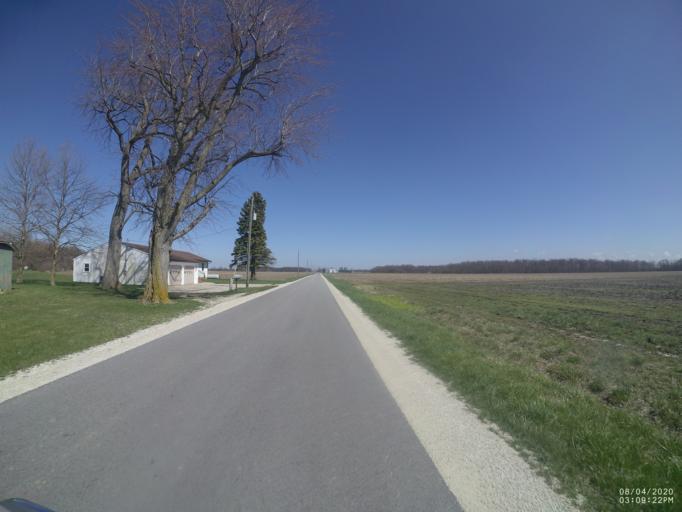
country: US
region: Ohio
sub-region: Sandusky County
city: Stony Prairie
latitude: 41.2823
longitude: -83.2266
